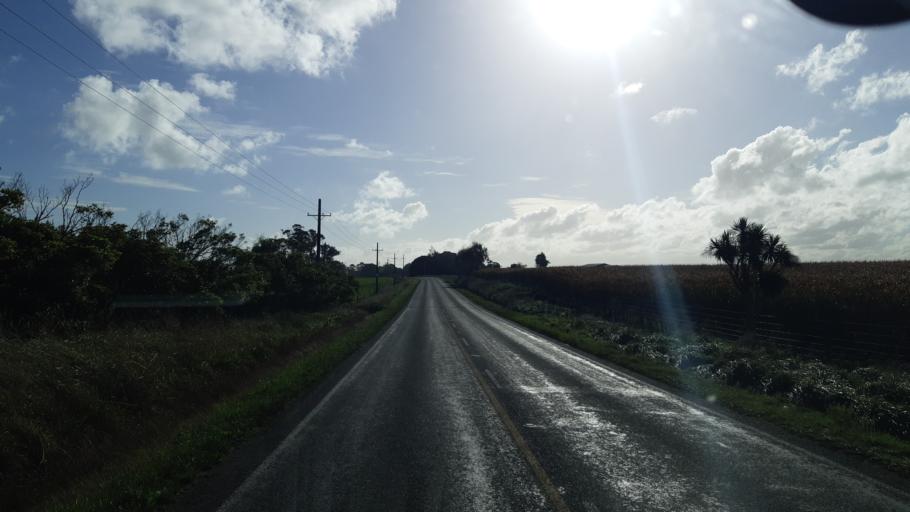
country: NZ
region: Manawatu-Wanganui
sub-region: Wanganui District
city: Wanganui
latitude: -39.9562
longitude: 175.1723
